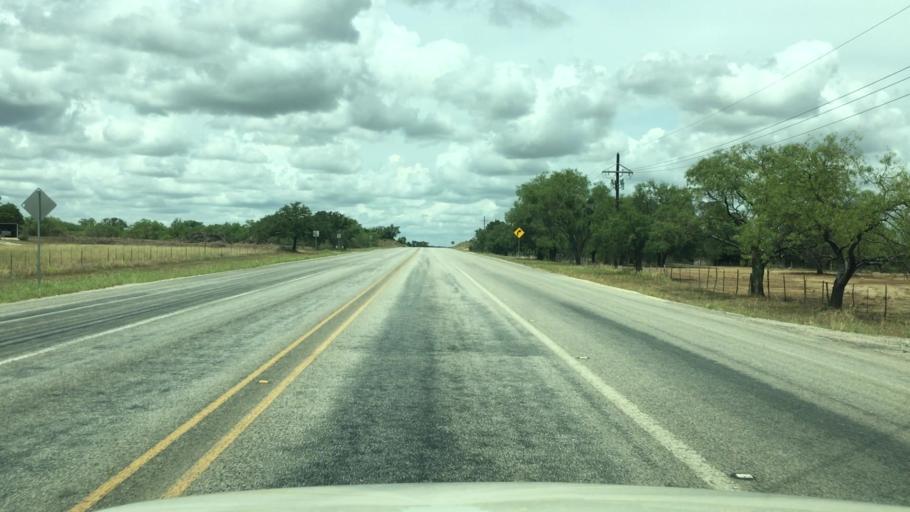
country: US
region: Texas
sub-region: McCulloch County
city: Brady
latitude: 31.0073
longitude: -99.2043
